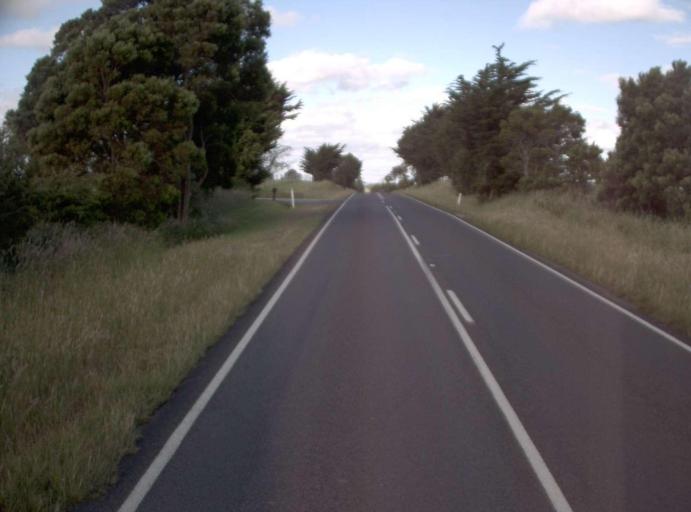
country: AU
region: Victoria
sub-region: Bass Coast
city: North Wonthaggi
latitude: -38.5359
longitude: 145.8697
